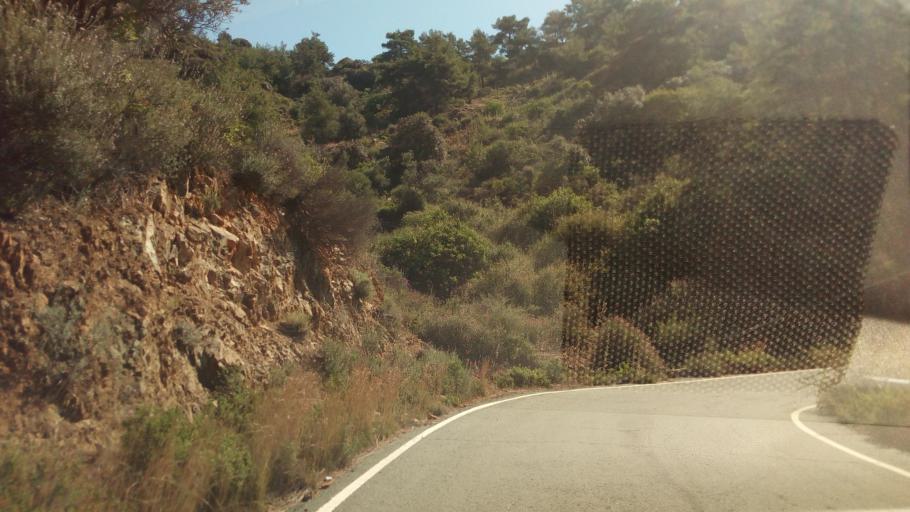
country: CY
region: Lefkosia
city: Lythrodontas
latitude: 34.8889
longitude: 33.2231
